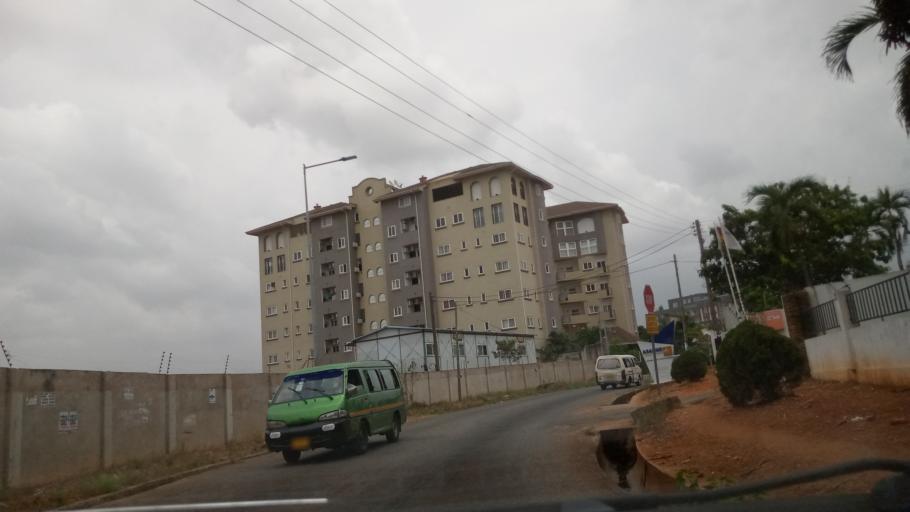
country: GH
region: Greater Accra
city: Accra
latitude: 5.6034
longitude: -0.1883
